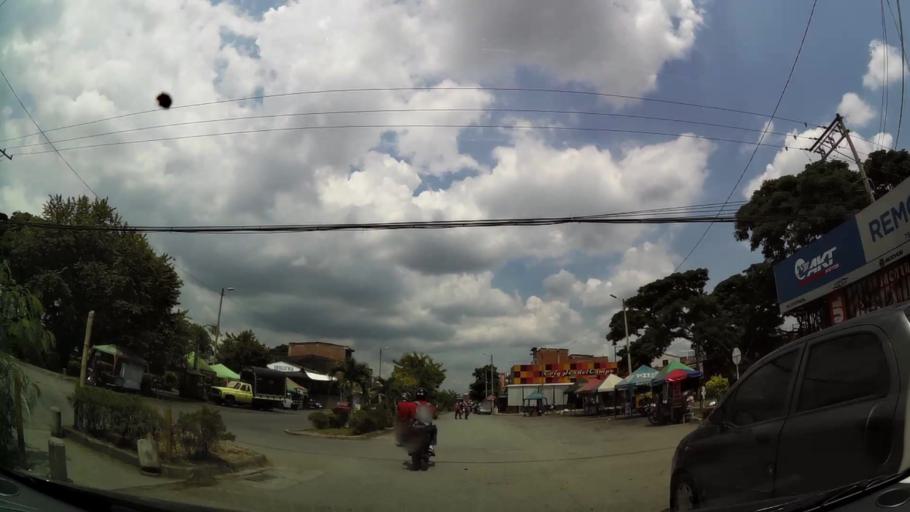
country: CO
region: Valle del Cauca
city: Cali
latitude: 3.4560
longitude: -76.4695
